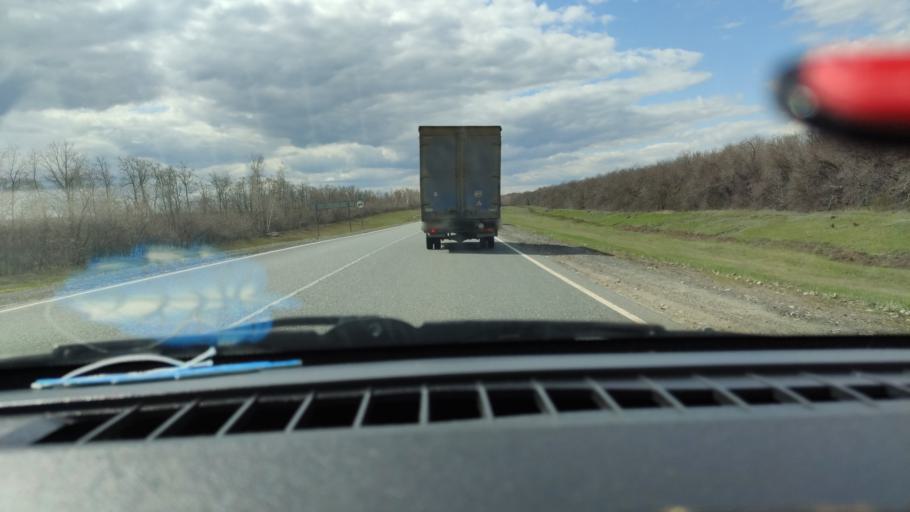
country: RU
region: Saratov
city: Balakovo
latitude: 52.1028
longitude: 47.7383
